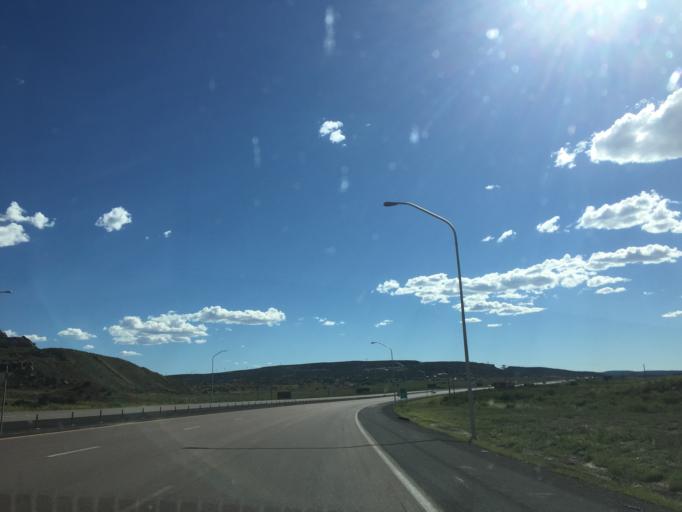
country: US
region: New Mexico
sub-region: McKinley County
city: Gallup
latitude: 35.5019
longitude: -108.8346
